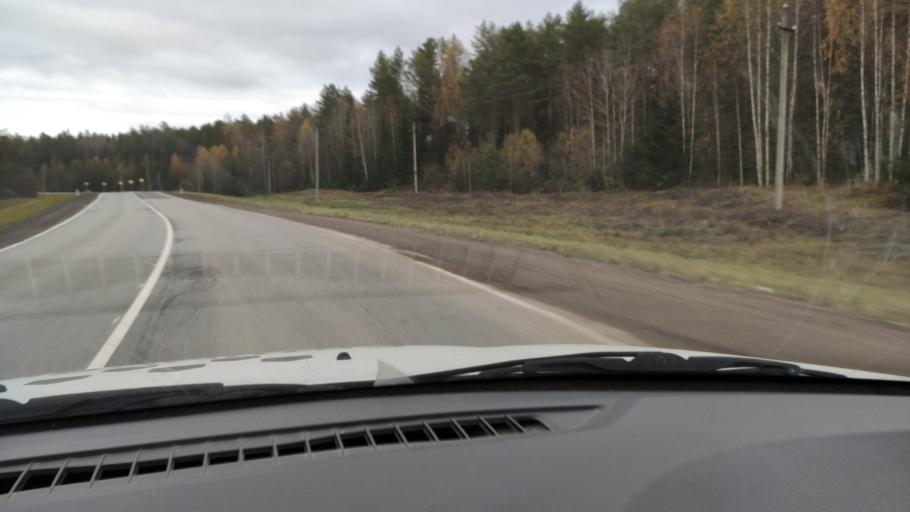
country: RU
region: Kirov
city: Belaya Kholunitsa
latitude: 58.8288
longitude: 50.6741
